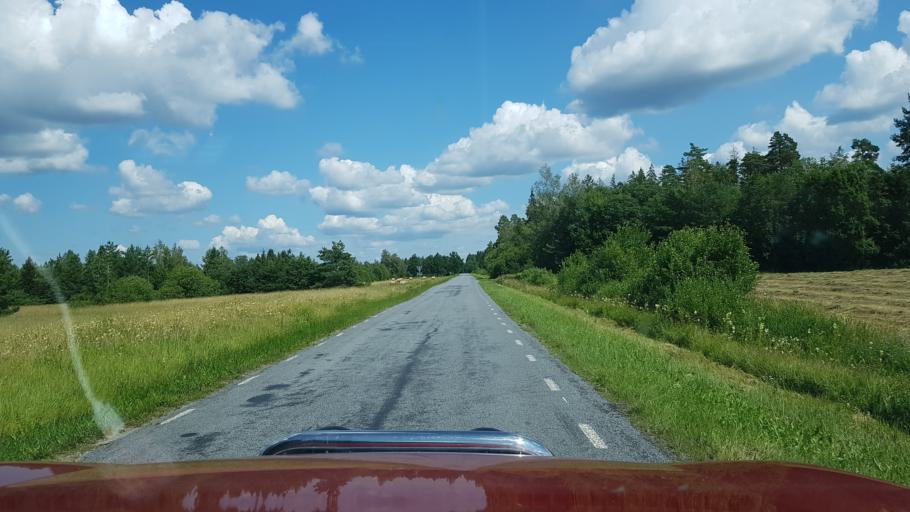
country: EE
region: Raplamaa
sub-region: Maerjamaa vald
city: Marjamaa
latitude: 58.7637
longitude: 24.4229
